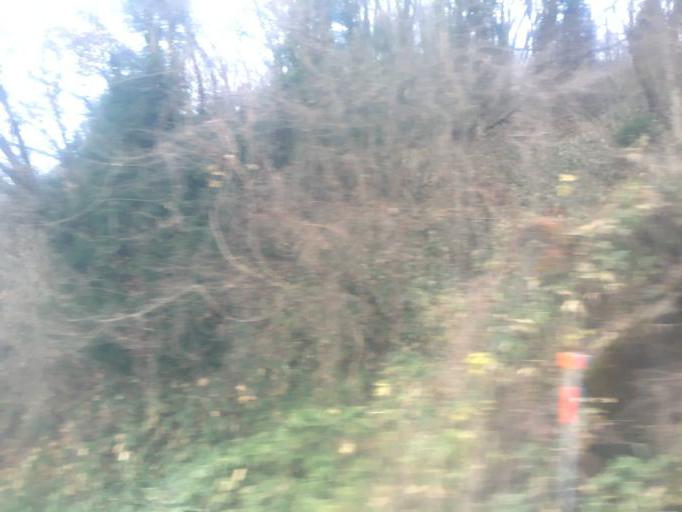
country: JP
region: Akita
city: Noshiromachi
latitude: 40.2115
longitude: 140.1367
